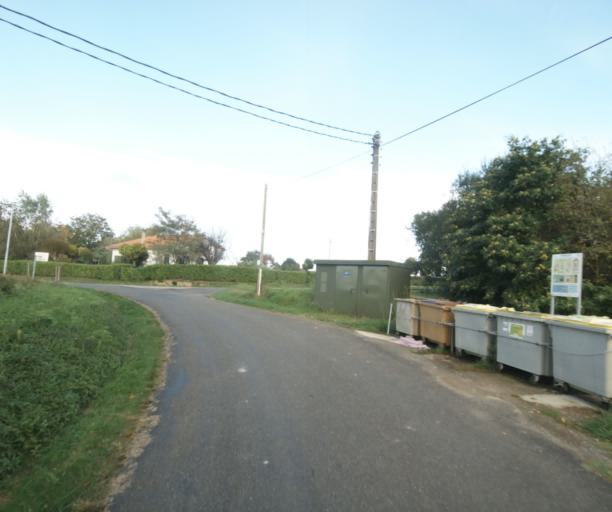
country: FR
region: Midi-Pyrenees
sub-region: Departement du Gers
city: Le Houga
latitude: 43.8546
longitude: -0.1418
